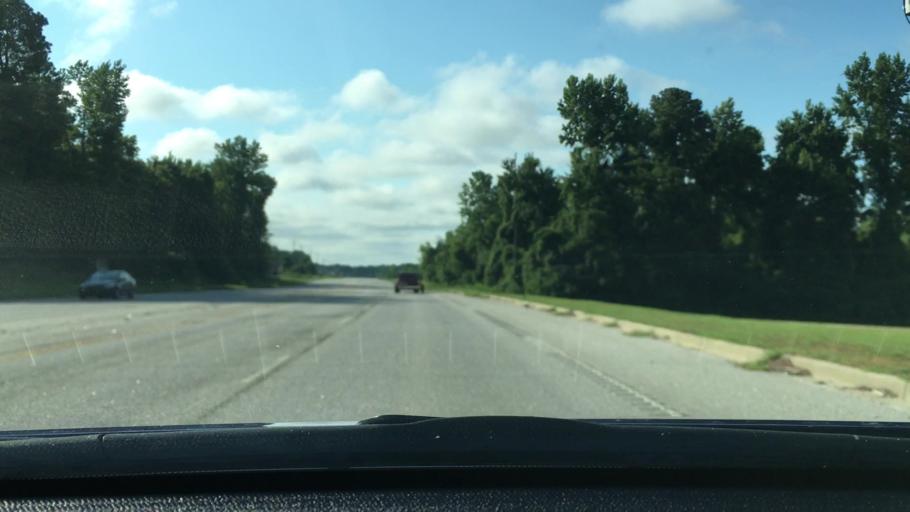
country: US
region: South Carolina
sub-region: Clarendon County
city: Manning
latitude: 33.7484
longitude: -80.2188
